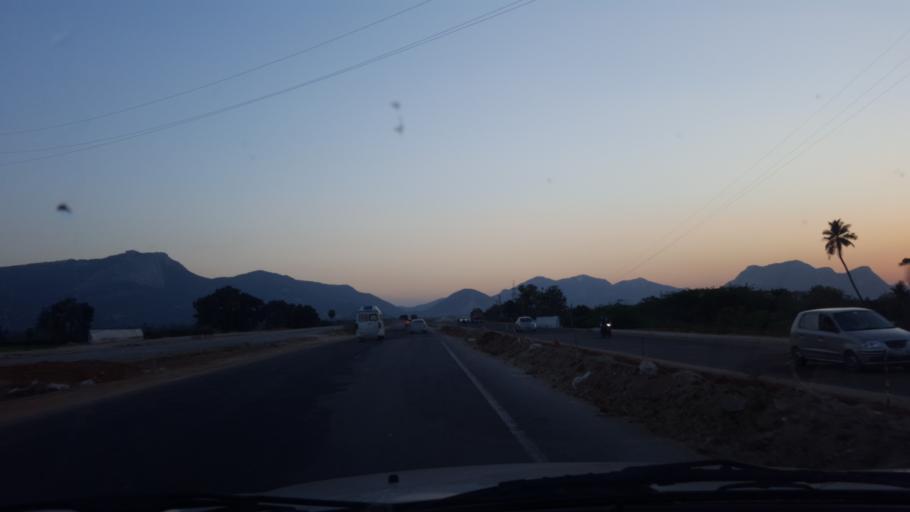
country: IN
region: Andhra Pradesh
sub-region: Chittoor
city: Narasingapuram
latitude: 13.5955
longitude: 79.3482
